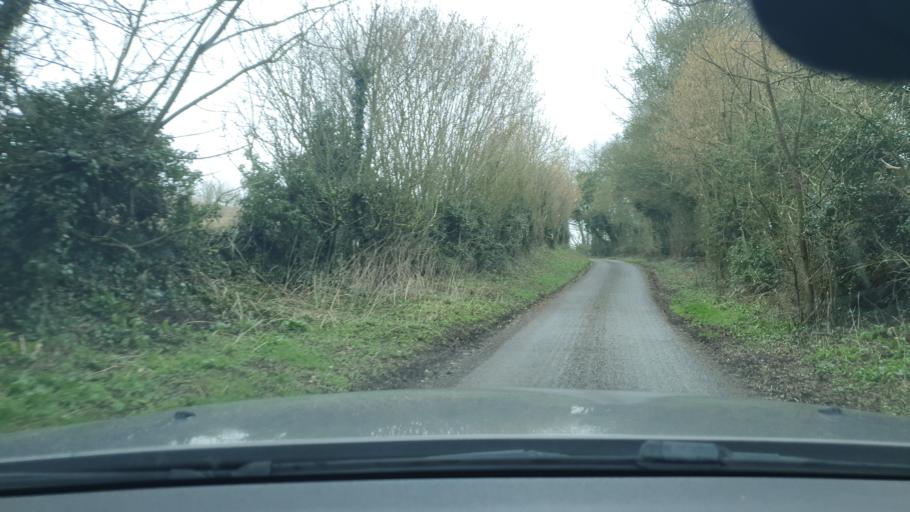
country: GB
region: England
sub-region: Wiltshire
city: Ramsbury
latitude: 51.4657
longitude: -1.6015
